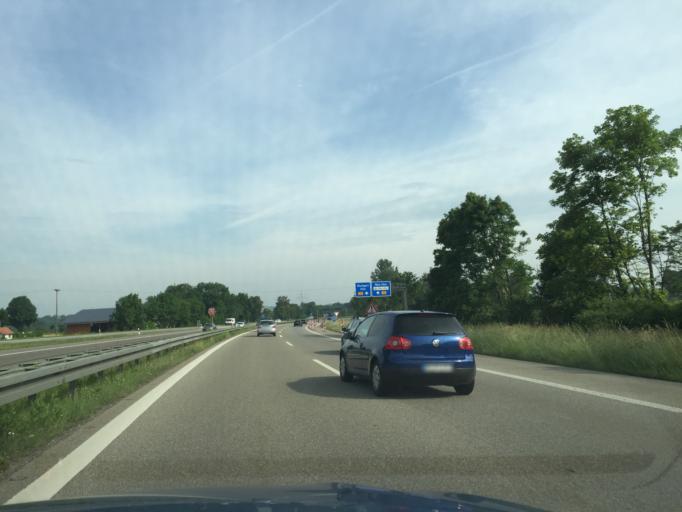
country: DE
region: Baden-Wuerttemberg
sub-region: Tuebingen Region
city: Ulm
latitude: 48.3729
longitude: 9.9940
